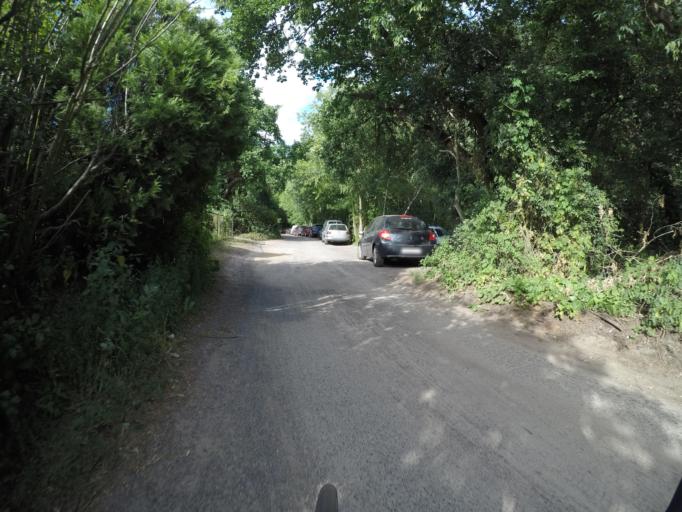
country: DE
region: Berlin
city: Baumschulenweg
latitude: 52.4568
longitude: 13.4803
